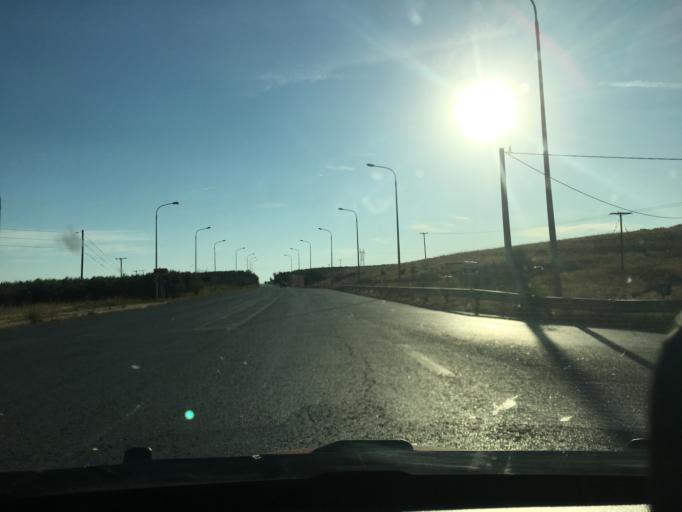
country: GR
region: Central Macedonia
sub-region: Nomos Chalkidikis
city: Olynthos
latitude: 40.2752
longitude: 23.3464
